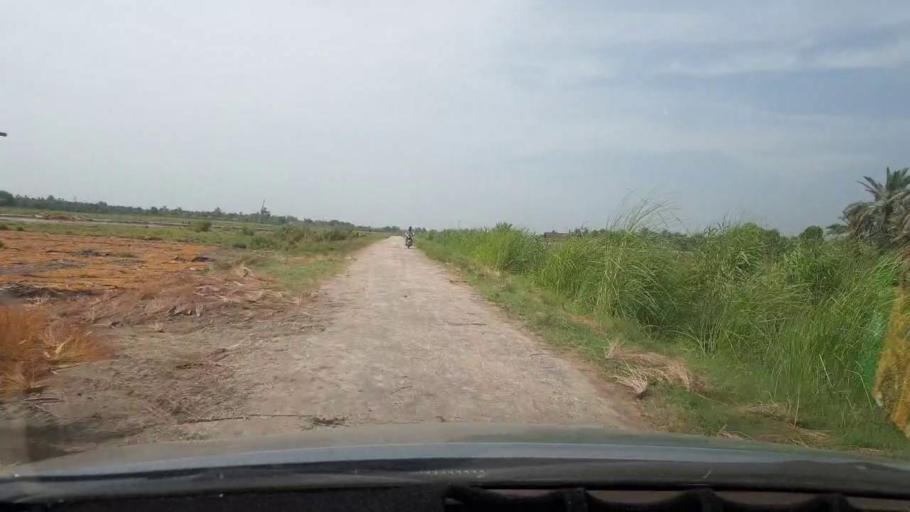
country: PK
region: Sindh
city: Khairpur
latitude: 27.4778
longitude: 68.7445
